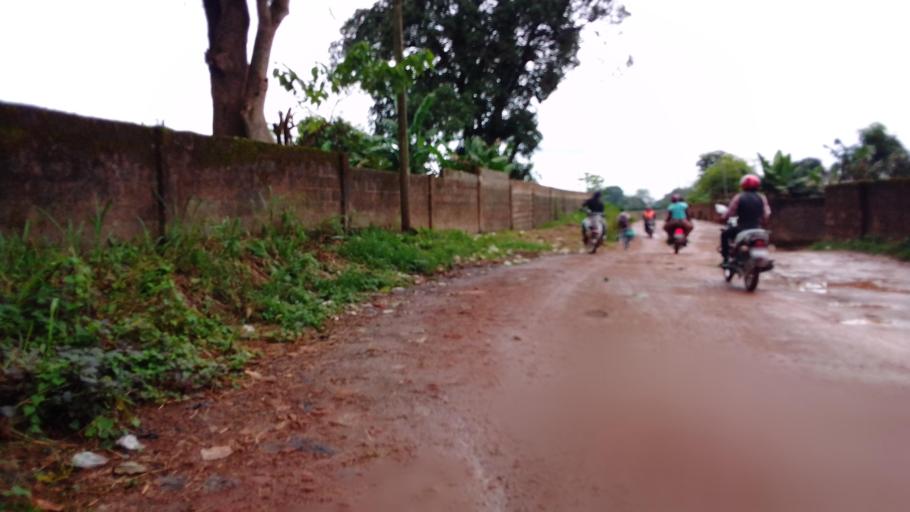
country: SL
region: Eastern Province
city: Kenema
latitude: 7.8734
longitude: -11.1799
